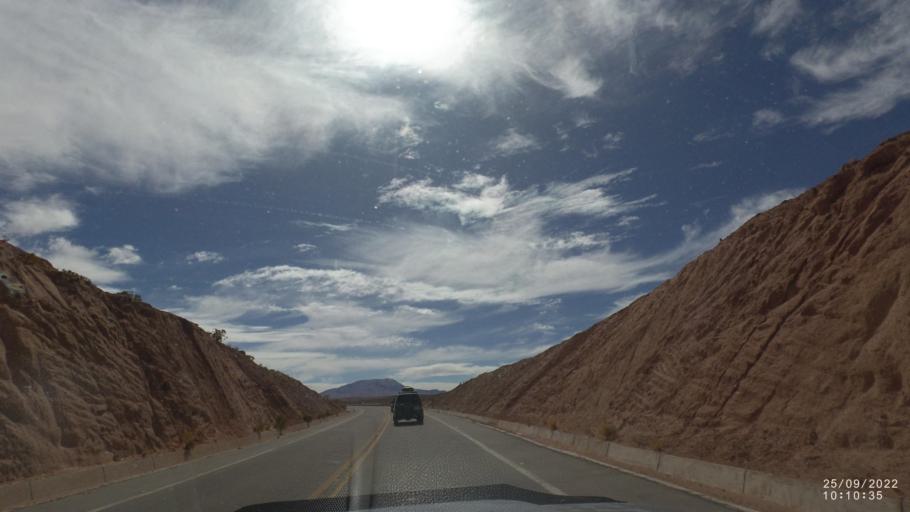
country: BO
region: Potosi
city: Colchani
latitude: -20.1108
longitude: -66.9121
